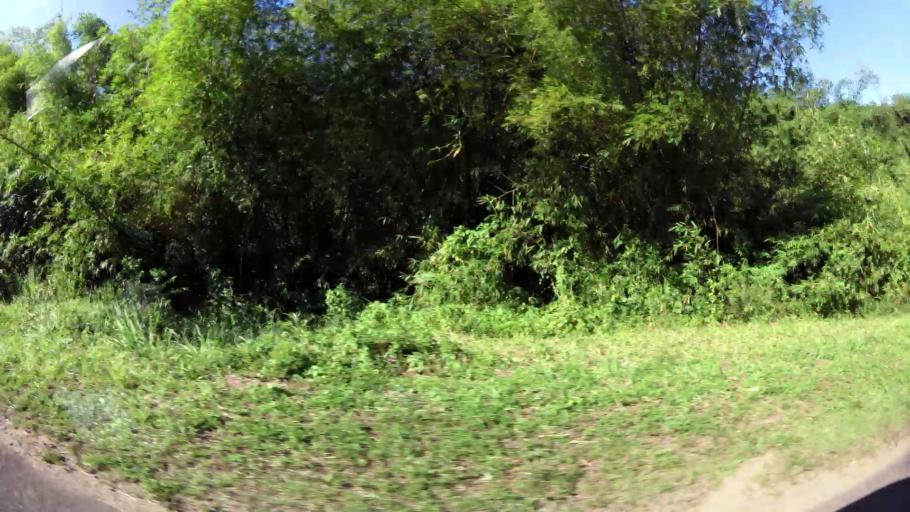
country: GF
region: Guyane
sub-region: Guyane
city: Matoury
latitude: 4.8620
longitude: -52.2721
